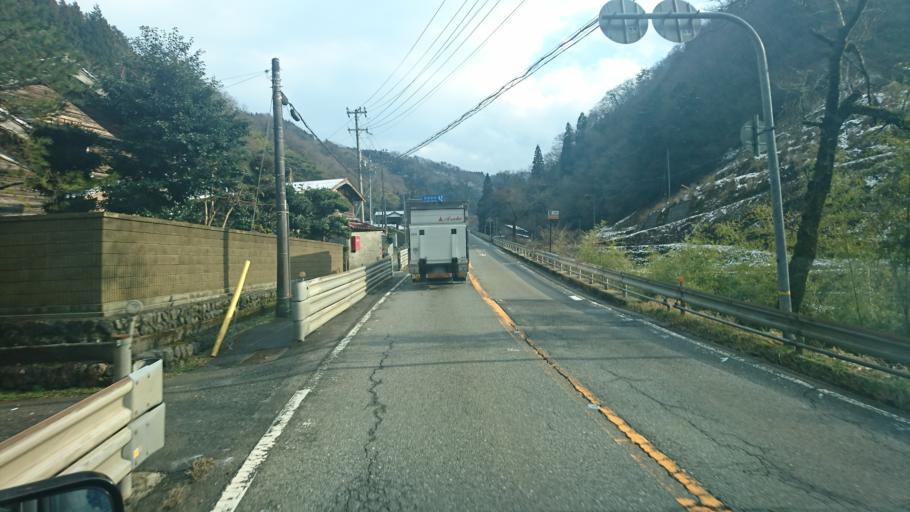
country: JP
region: Tottori
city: Tottori
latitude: 35.5243
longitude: 134.5208
